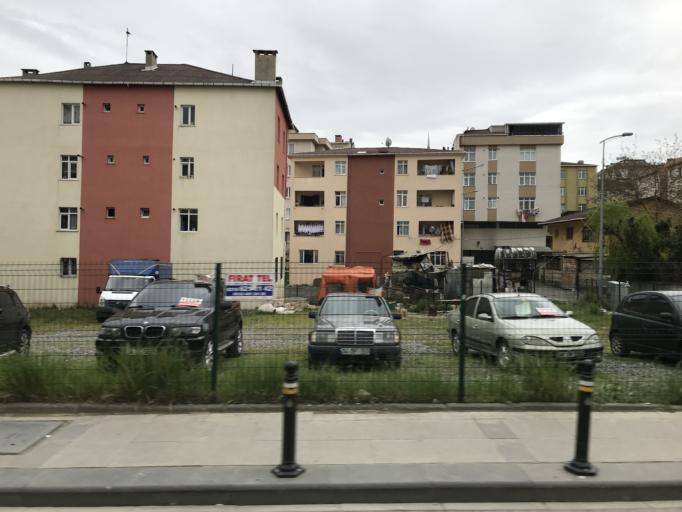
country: TR
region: Istanbul
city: Umraniye
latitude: 41.0108
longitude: 29.1701
